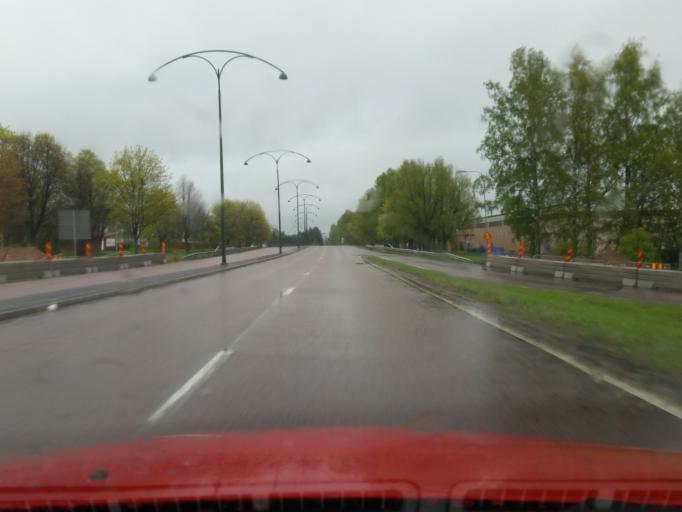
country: SE
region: Dalarna
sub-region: Borlange Kommun
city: Borlaenge
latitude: 60.4802
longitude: 15.4285
